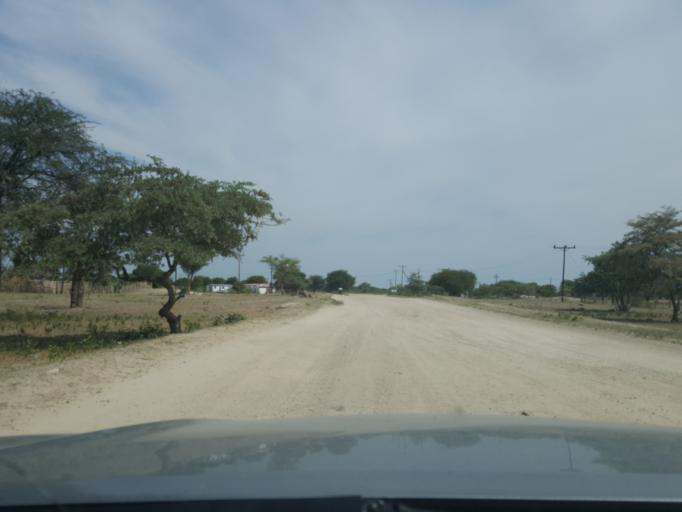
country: BW
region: North West
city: Shakawe
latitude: -18.3089
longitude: 21.8917
